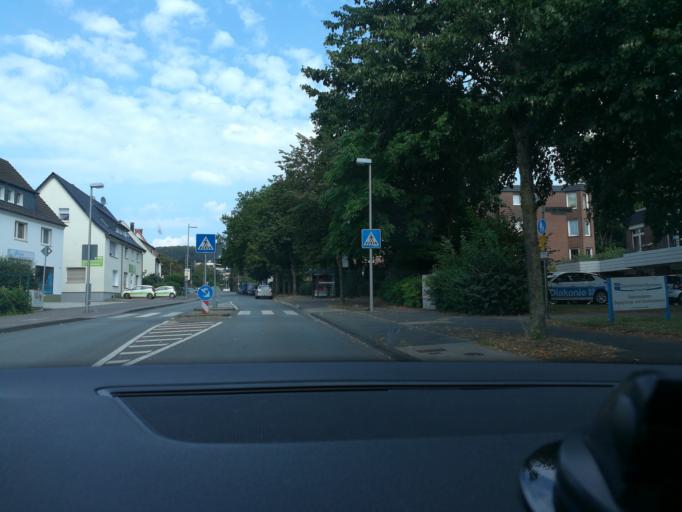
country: DE
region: North Rhine-Westphalia
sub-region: Regierungsbezirk Detmold
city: Bielefeld
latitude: 51.9836
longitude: 8.5106
